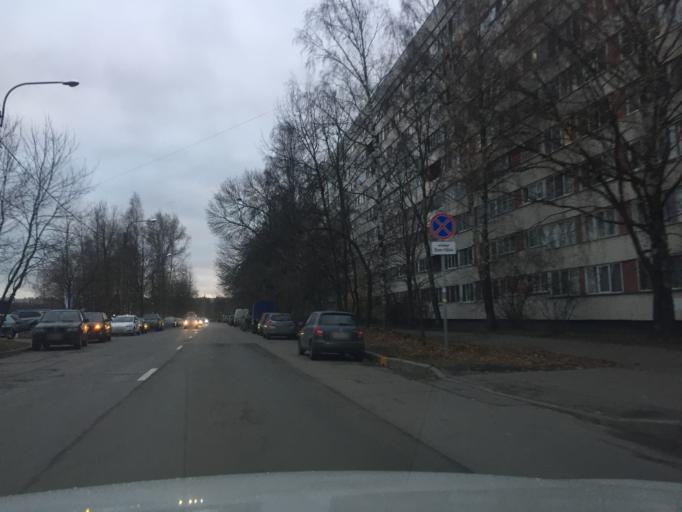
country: RU
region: St.-Petersburg
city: Grazhdanka
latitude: 60.0241
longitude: 30.4281
